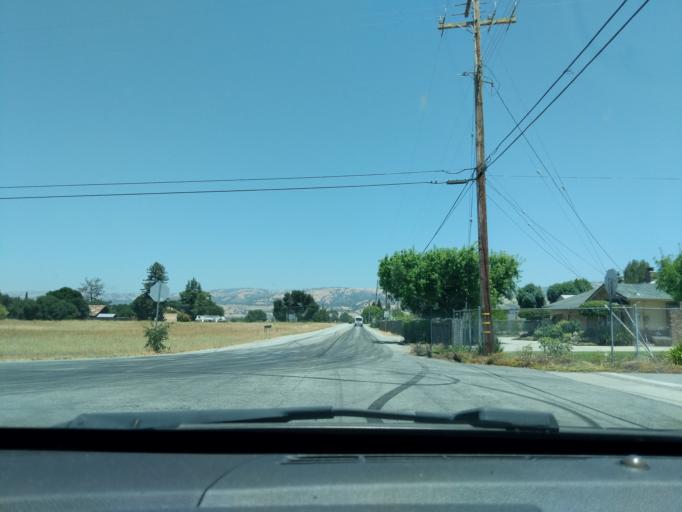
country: US
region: California
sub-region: Santa Clara County
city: San Martin
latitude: 37.0968
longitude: -121.6331
